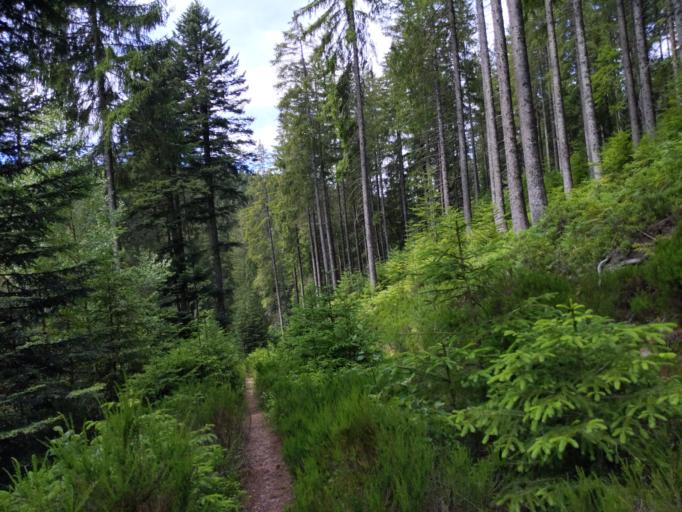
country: DE
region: Baden-Wuerttemberg
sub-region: Karlsruhe Region
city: Freudenstadt
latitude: 48.4378
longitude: 8.3718
